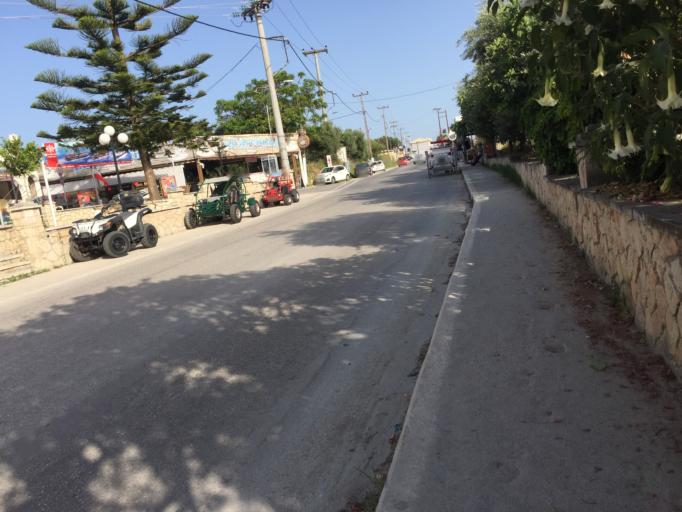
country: GR
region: Ionian Islands
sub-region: Nomos Zakynthou
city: Vanaton
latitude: 37.8182
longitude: 20.8623
